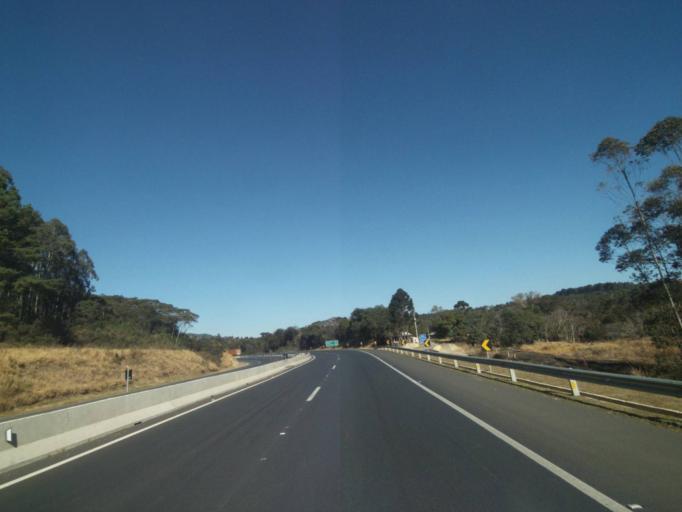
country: BR
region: Parana
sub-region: Tibagi
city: Tibagi
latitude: -24.7529
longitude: -50.5363
